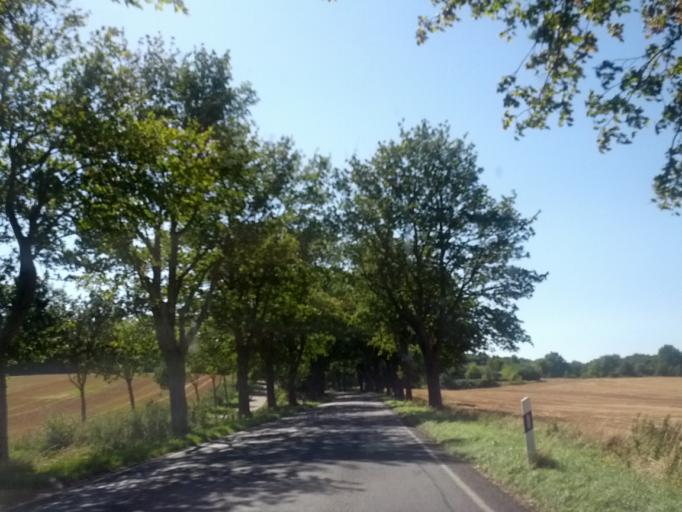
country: DE
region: Mecklenburg-Vorpommern
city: Bergen auf Ruegen
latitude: 54.4280
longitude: 13.4325
